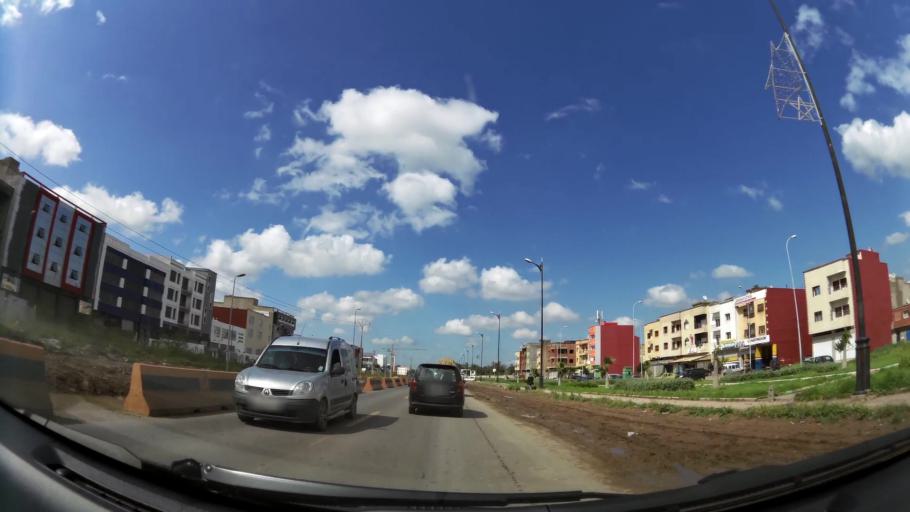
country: MA
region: Grand Casablanca
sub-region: Mediouna
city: Mediouna
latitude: 33.3999
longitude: -7.5346
